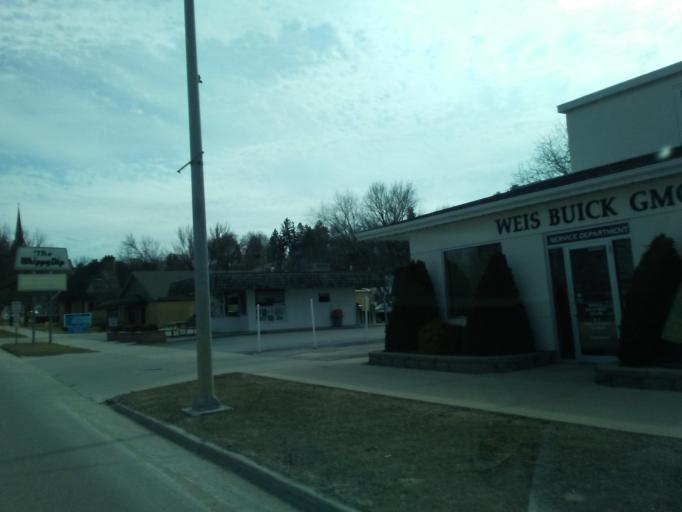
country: US
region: Iowa
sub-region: Winneshiek County
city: Decorah
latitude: 43.3052
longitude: -91.7945
